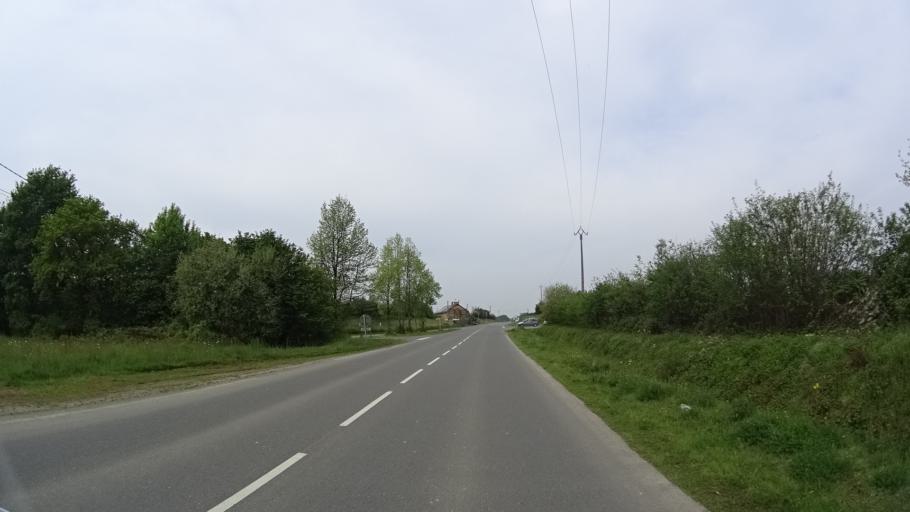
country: FR
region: Brittany
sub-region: Departement d'Ille-et-Vilaine
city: Vignoc
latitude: 48.2505
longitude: -1.7557
